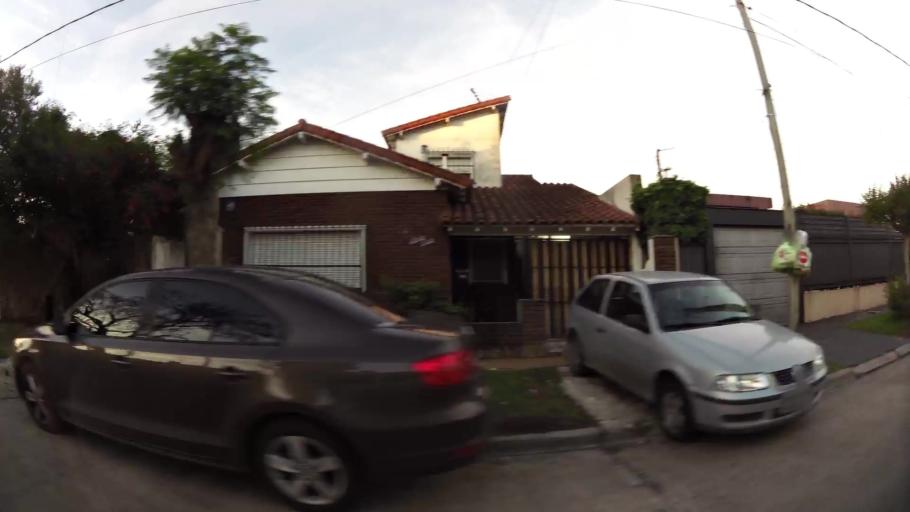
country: AR
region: Buenos Aires
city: Ituzaingo
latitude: -34.6504
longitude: -58.6541
